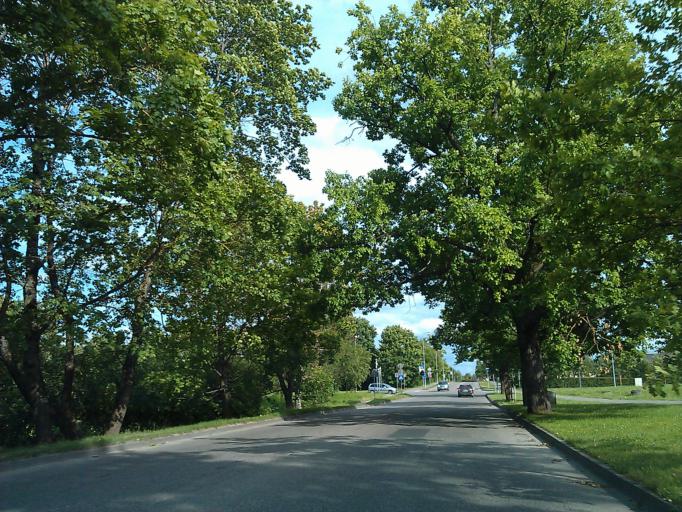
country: LV
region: Cesu Rajons
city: Cesis
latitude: 57.3080
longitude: 25.2810
